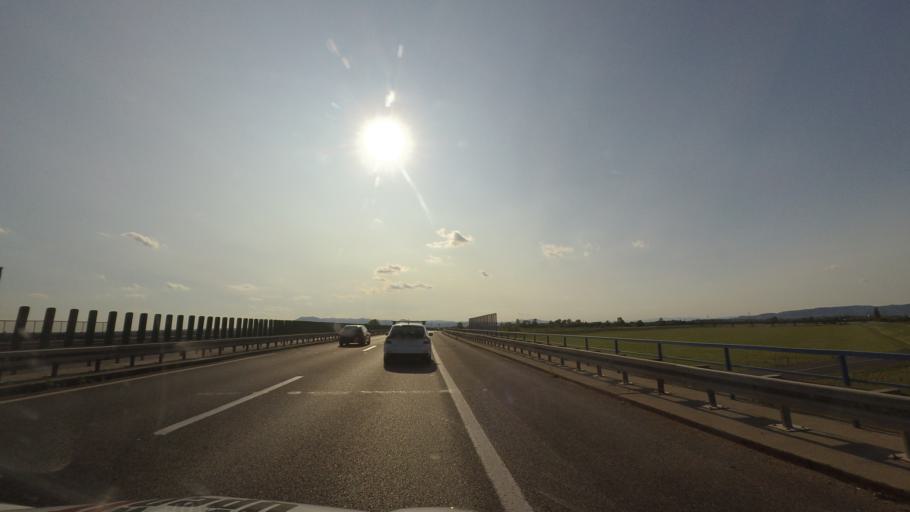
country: HR
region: Grad Zagreb
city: Zadvorsko
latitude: 45.7488
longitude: 15.9208
